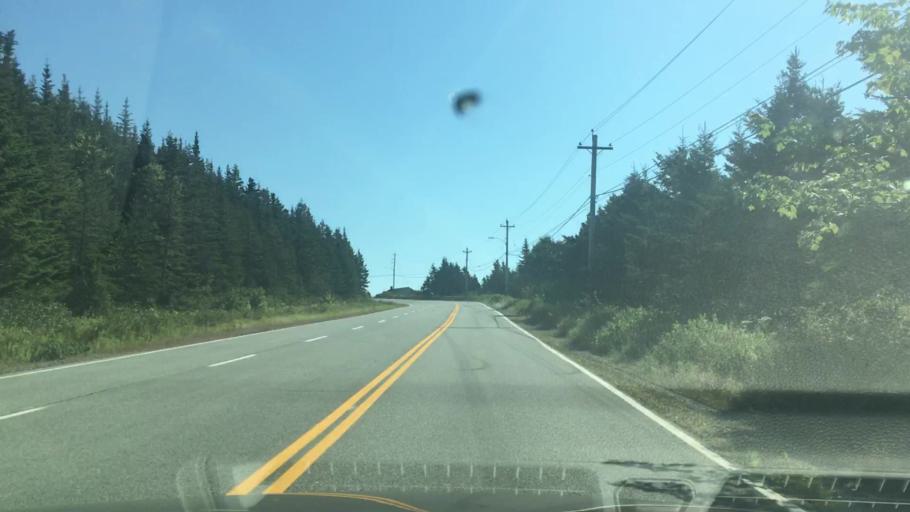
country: CA
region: Nova Scotia
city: New Glasgow
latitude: 44.8142
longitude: -62.6355
